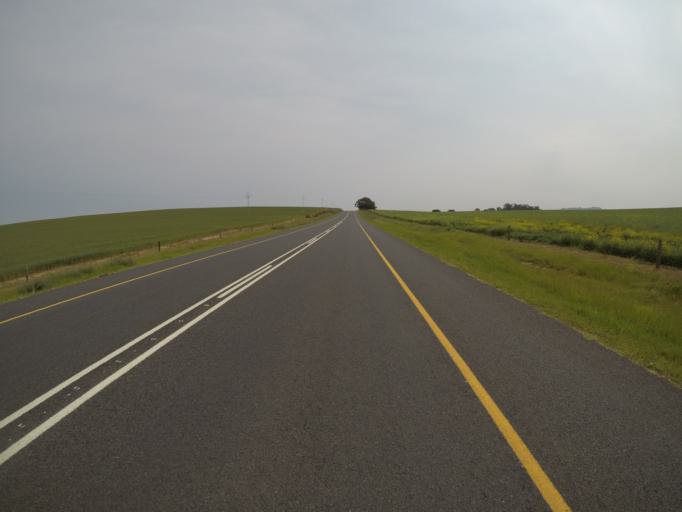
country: ZA
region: Western Cape
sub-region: West Coast District Municipality
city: Malmesbury
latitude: -33.5066
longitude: 18.8405
